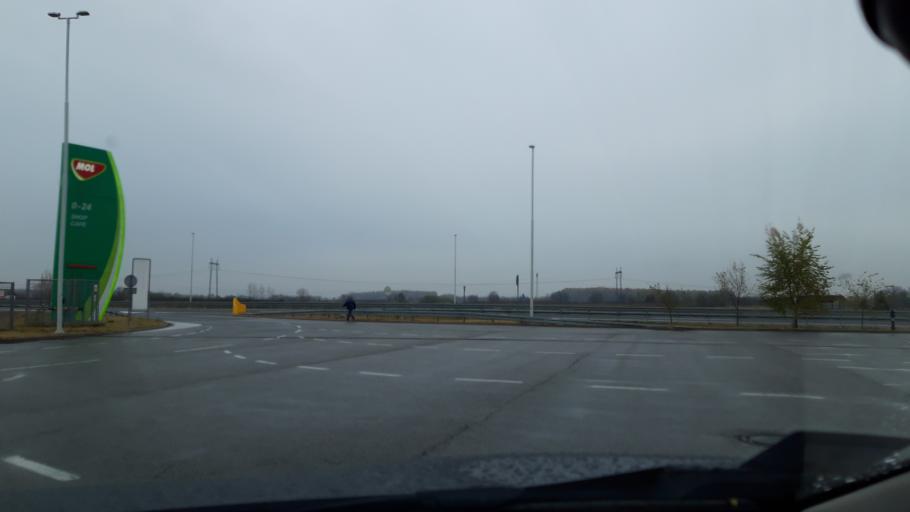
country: HU
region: Csongrad
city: Roszke
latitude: 46.1646
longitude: 19.9568
